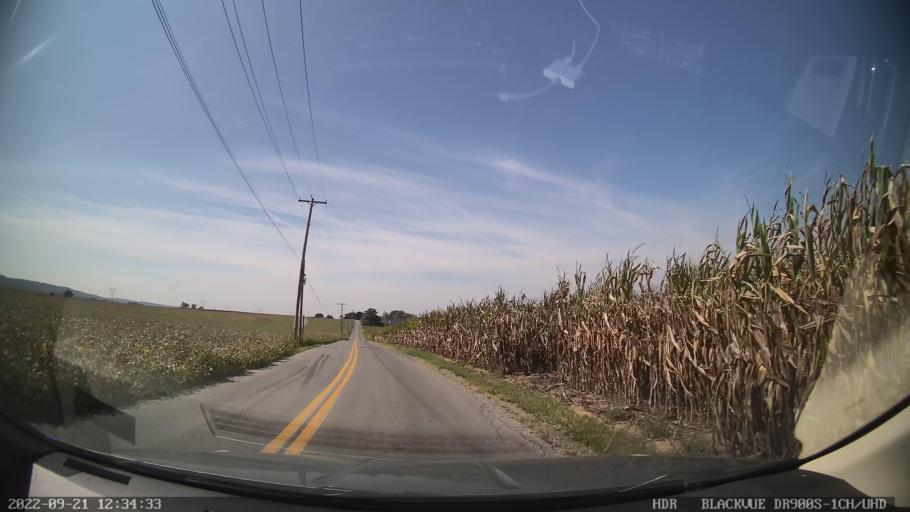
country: US
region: Pennsylvania
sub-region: Berks County
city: Kutztown
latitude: 40.4967
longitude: -75.7571
